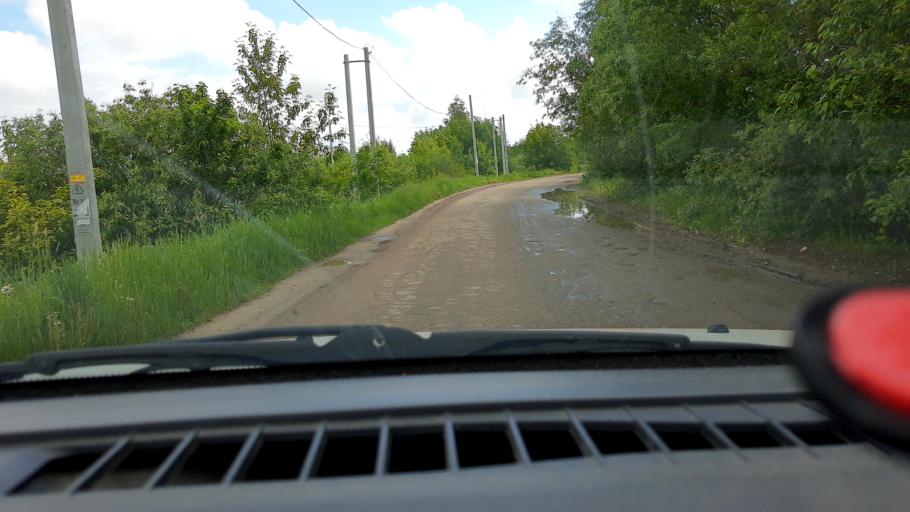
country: RU
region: Nizjnij Novgorod
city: Neklyudovo
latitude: 56.4229
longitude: 43.9565
